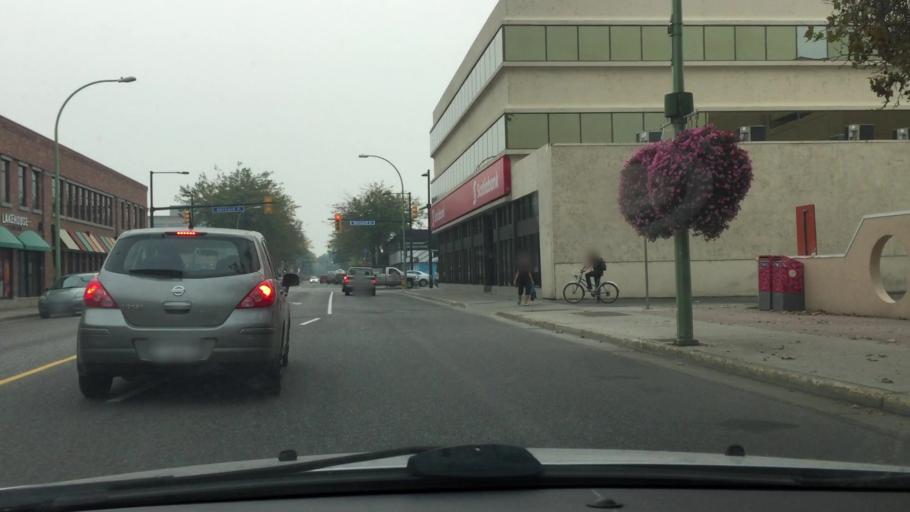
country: CA
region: British Columbia
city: Kelowna
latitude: 49.8870
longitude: -119.4936
